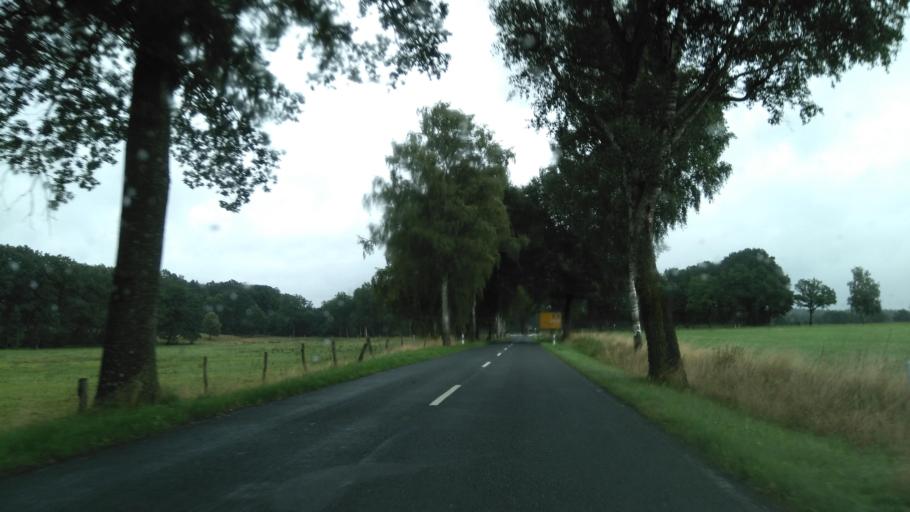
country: DE
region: Lower Saxony
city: Bomlitz
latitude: 52.8983
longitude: 9.6099
